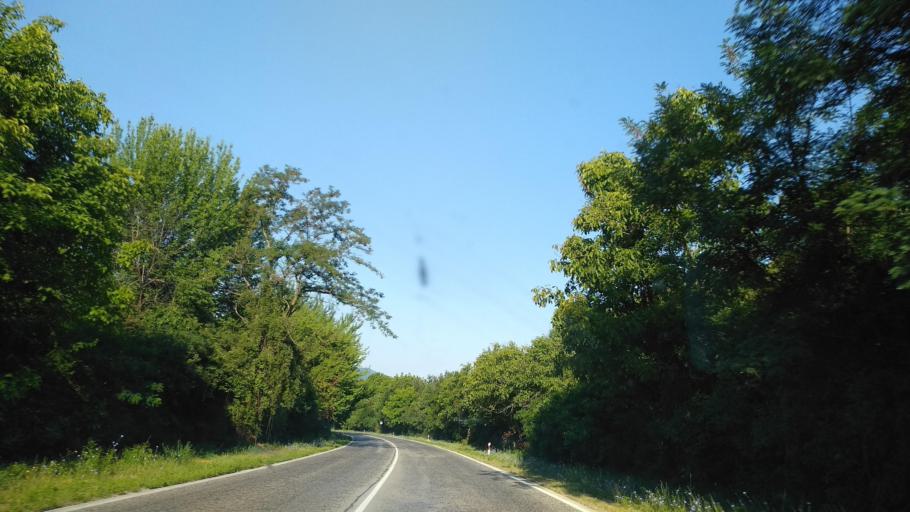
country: BG
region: Lovech
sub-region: Obshtina Lovech
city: Lovech
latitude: 43.0481
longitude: 24.7599
